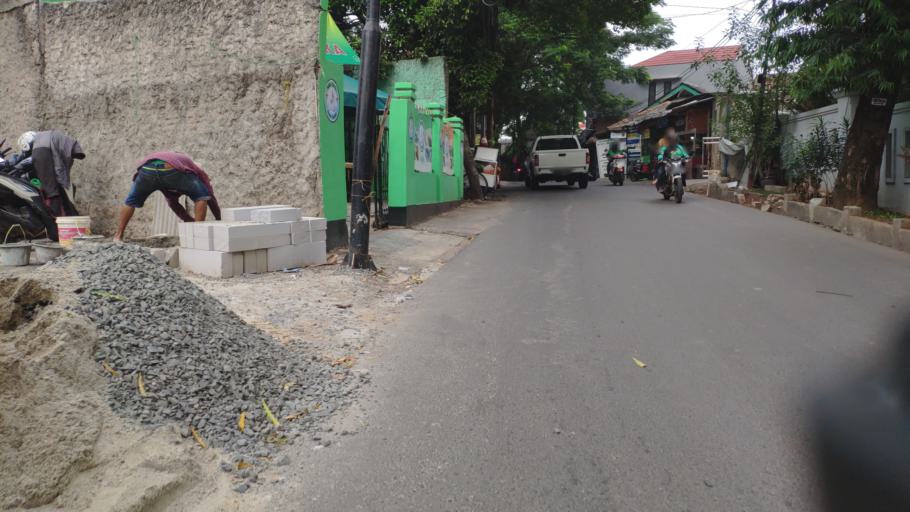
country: ID
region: Jakarta Raya
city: Jakarta
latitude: -6.3011
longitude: 106.8322
